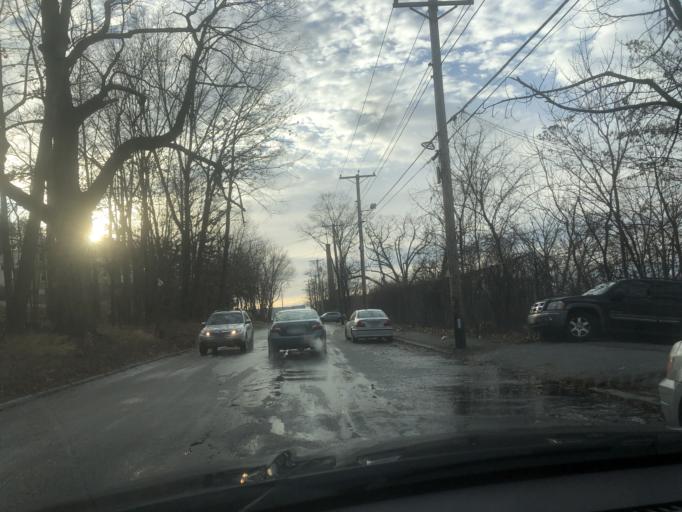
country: US
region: Massachusetts
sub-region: Essex County
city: Lawrence
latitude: 42.7126
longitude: -71.1514
